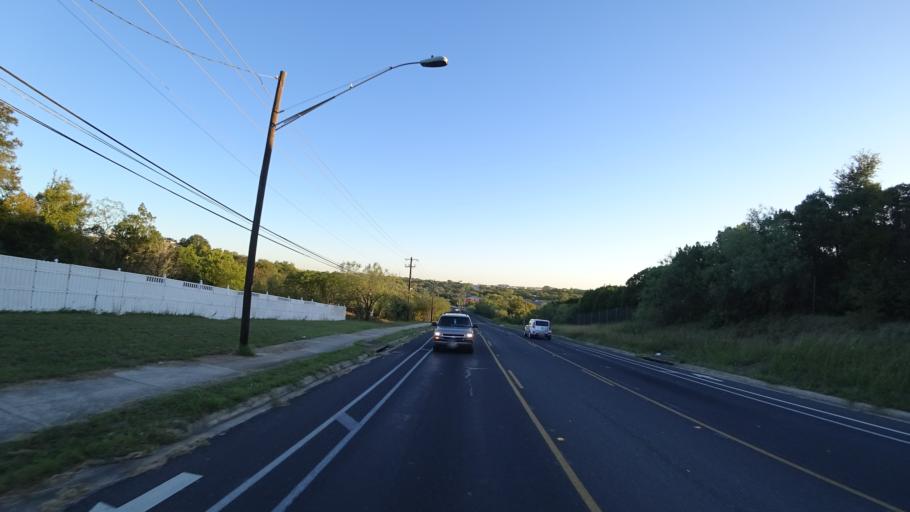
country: US
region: Texas
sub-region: Travis County
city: Austin
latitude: 30.3038
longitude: -97.6712
